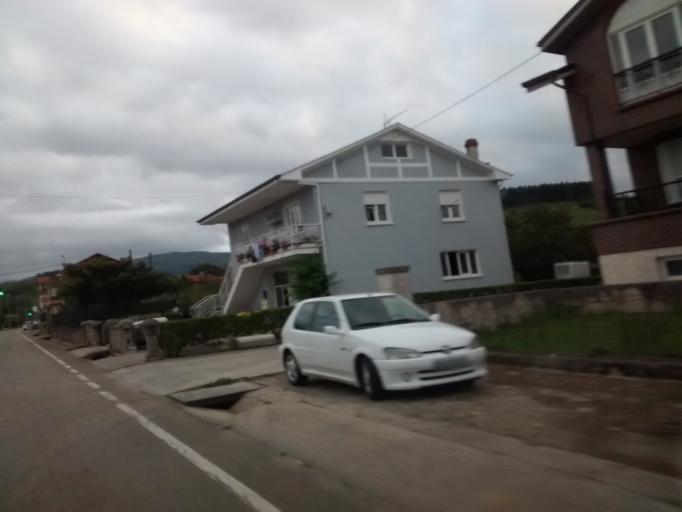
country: ES
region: Cantabria
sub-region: Provincia de Cantabria
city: Entrambasaguas
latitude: 43.3739
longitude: -3.7180
